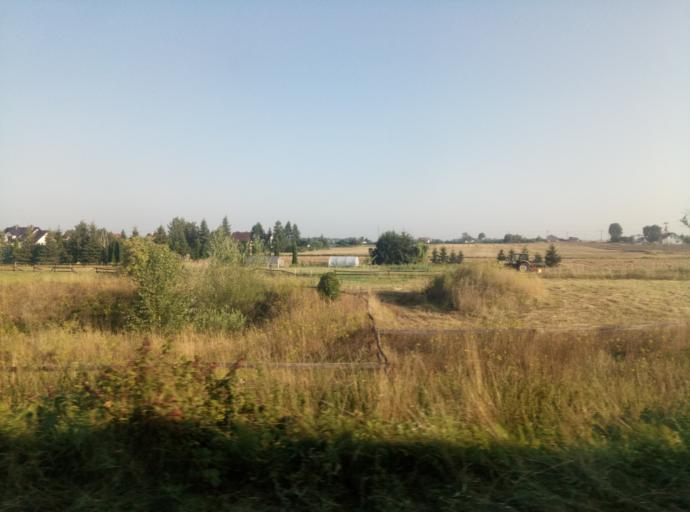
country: PL
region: Kujawsko-Pomorskie
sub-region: Powiat golubsko-dobrzynski
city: Kowalewo Pomorskie
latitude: 53.1425
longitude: 18.8154
